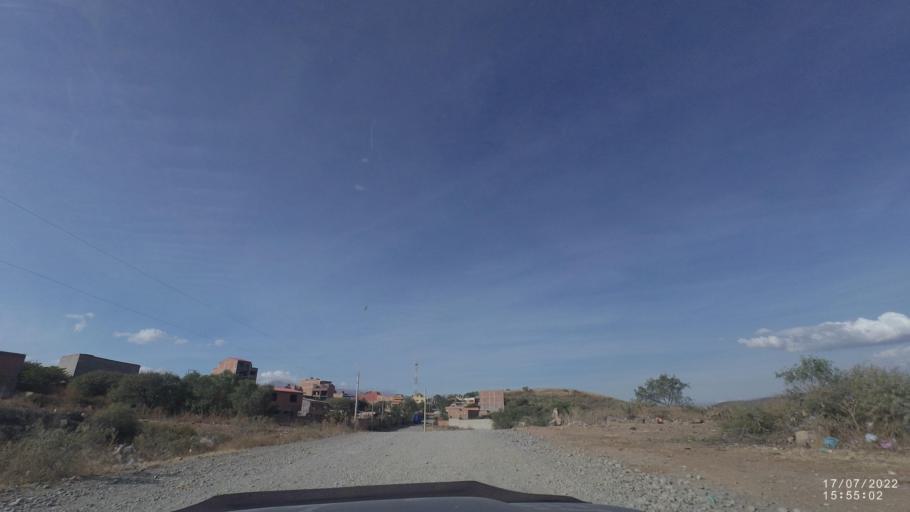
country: BO
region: Cochabamba
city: Sipe Sipe
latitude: -17.4252
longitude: -66.2888
